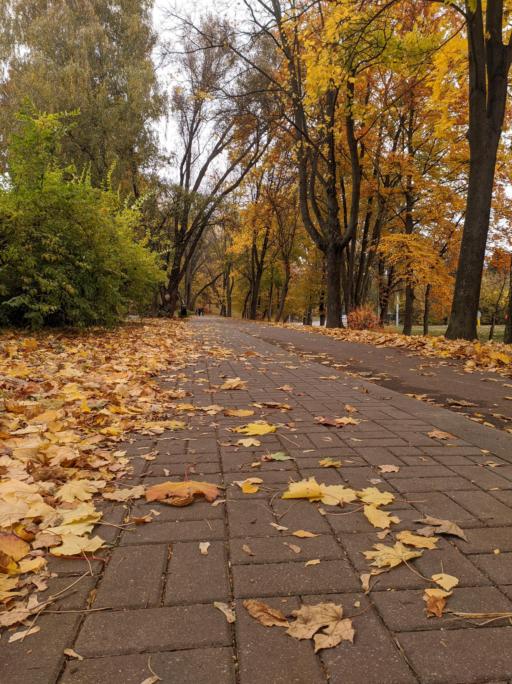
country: PL
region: Lublin Voivodeship
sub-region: Powiat lubelski
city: Lublin
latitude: 51.2419
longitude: 22.5312
